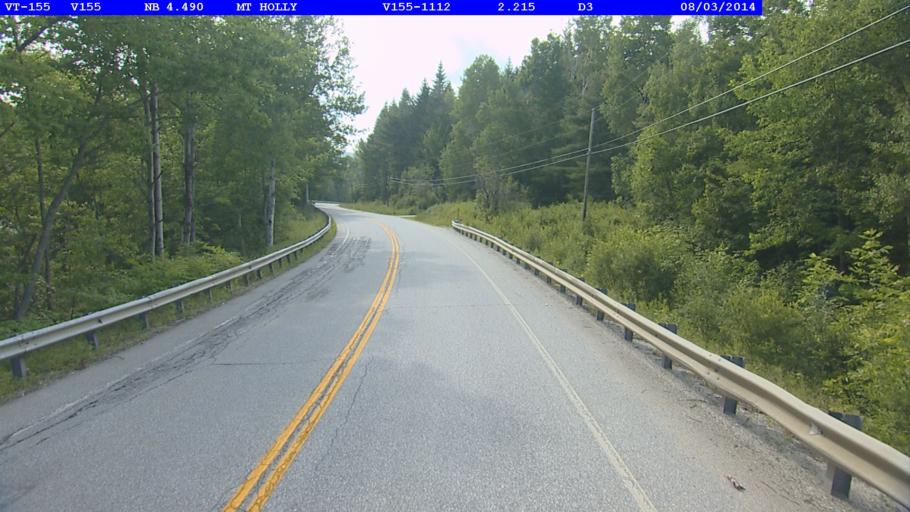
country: US
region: Vermont
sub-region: Windsor County
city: Chester
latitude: 43.3914
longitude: -72.8090
